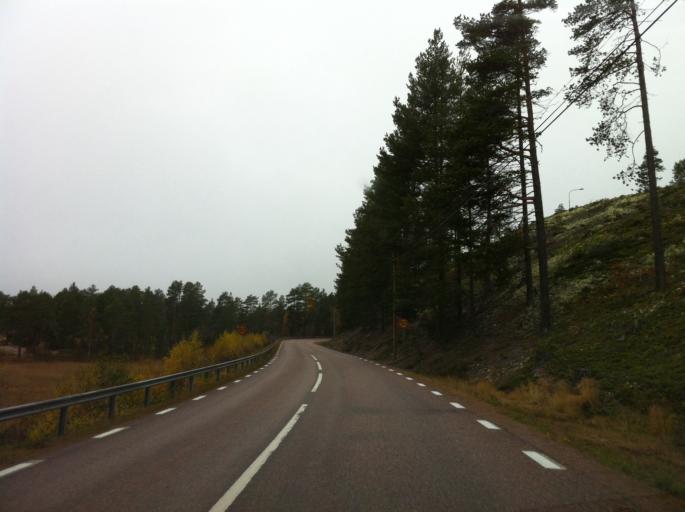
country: NO
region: Hedmark
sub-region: Trysil
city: Innbygda
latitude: 61.8554
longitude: 12.7379
